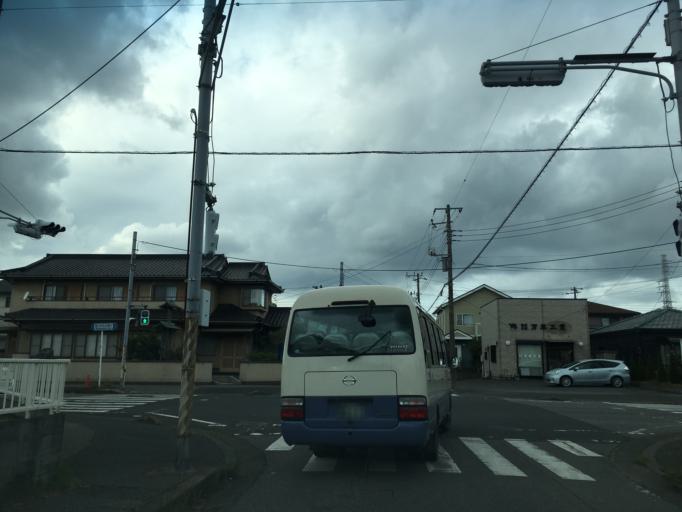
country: JP
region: Chiba
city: Kimitsu
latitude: 35.3322
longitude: 139.8748
